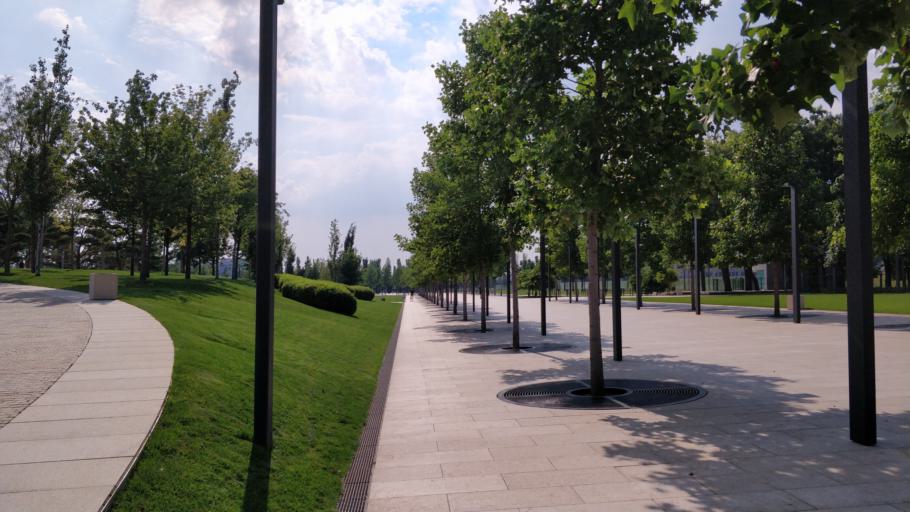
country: RU
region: Krasnodarskiy
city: Krasnodar
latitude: 45.0423
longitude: 39.0359
